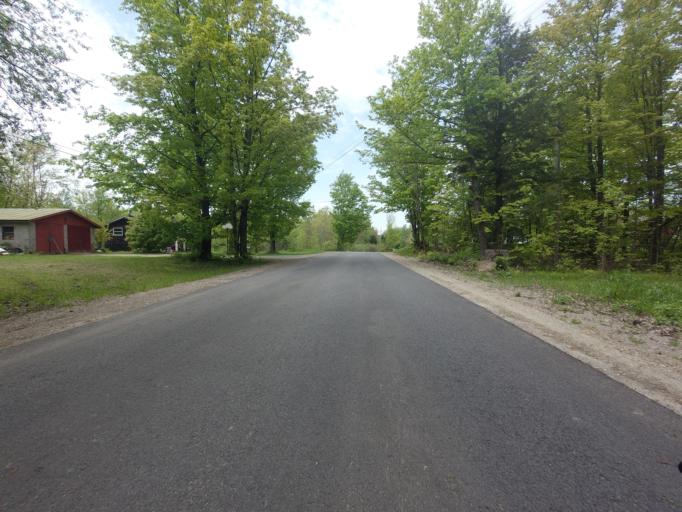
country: US
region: New York
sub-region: St. Lawrence County
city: Hannawa Falls
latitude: 44.5529
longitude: -74.9507
